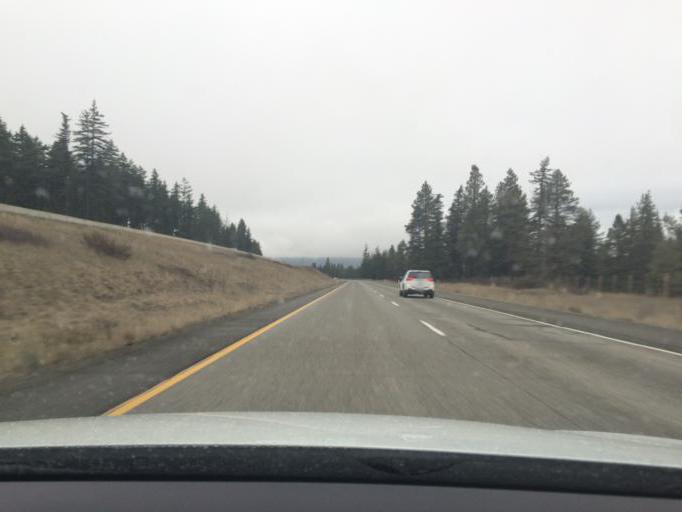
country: US
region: Washington
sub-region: Kittitas County
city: Cle Elum
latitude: 47.1424
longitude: -120.8137
